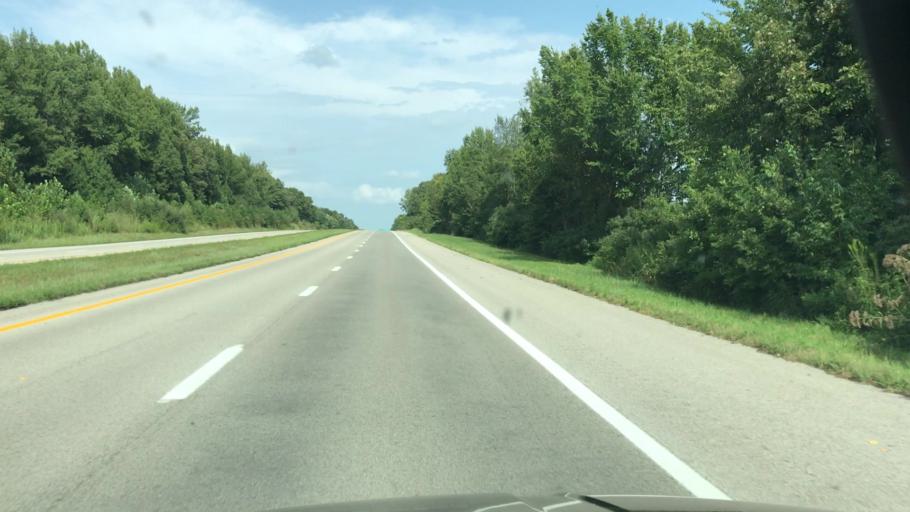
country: US
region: Kentucky
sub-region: Hopkins County
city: Nortonville
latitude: 37.2071
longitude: -87.4989
